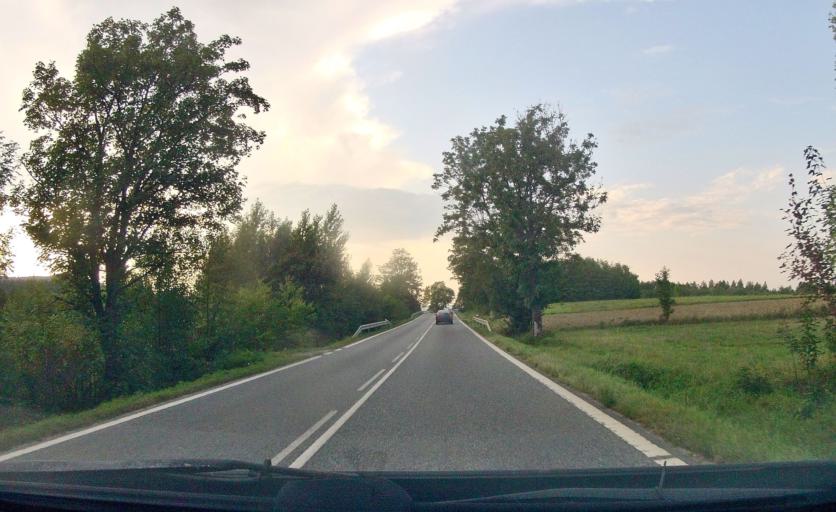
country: PL
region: Subcarpathian Voivodeship
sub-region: Powiat jasielski
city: Nowy Zmigrod
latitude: 49.5792
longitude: 21.5556
